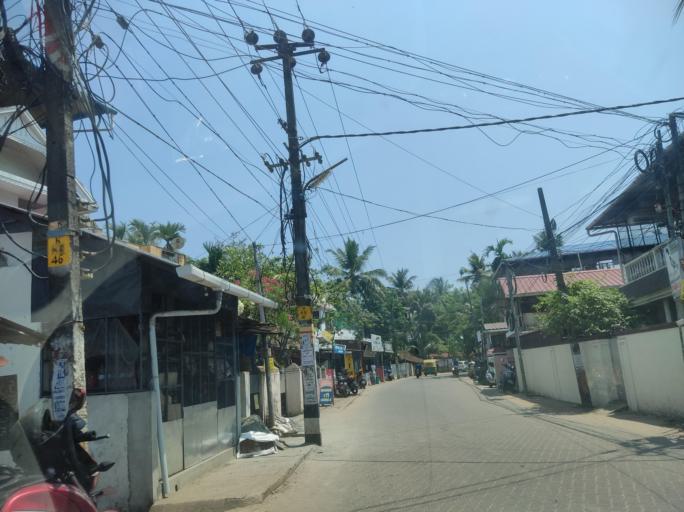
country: IN
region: Kerala
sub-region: Ernakulam
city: Cochin
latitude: 9.8921
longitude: 76.2850
